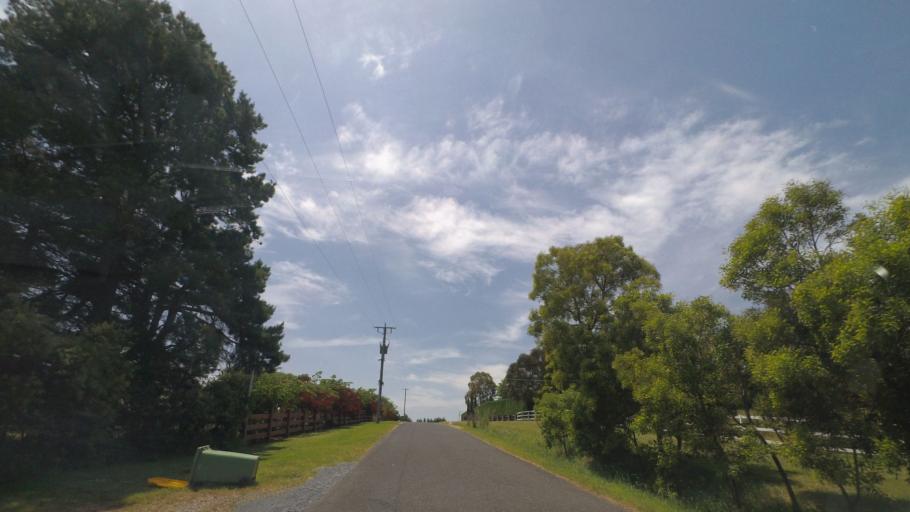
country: AU
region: Victoria
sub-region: Yarra Ranges
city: Chirnside Park
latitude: -37.7544
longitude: 145.3003
